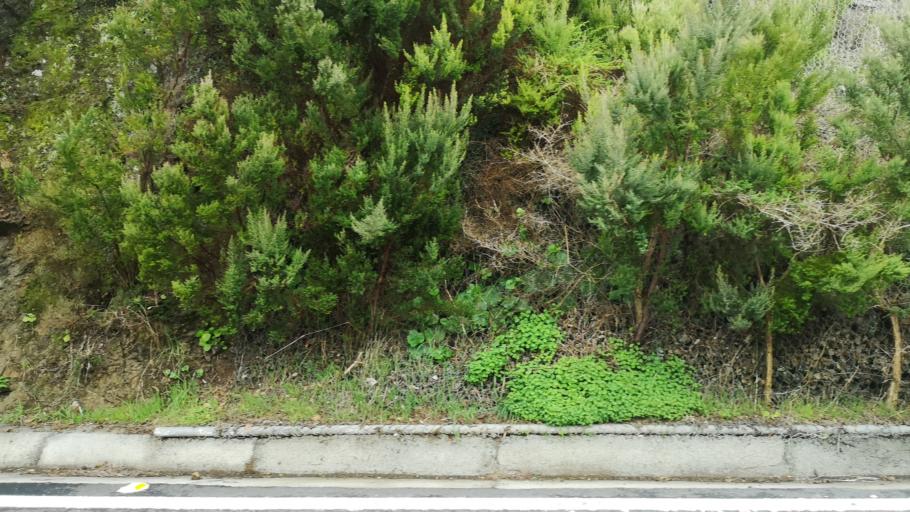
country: ES
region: Canary Islands
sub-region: Provincia de Santa Cruz de Tenerife
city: Alajero
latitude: 28.1150
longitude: -17.2428
